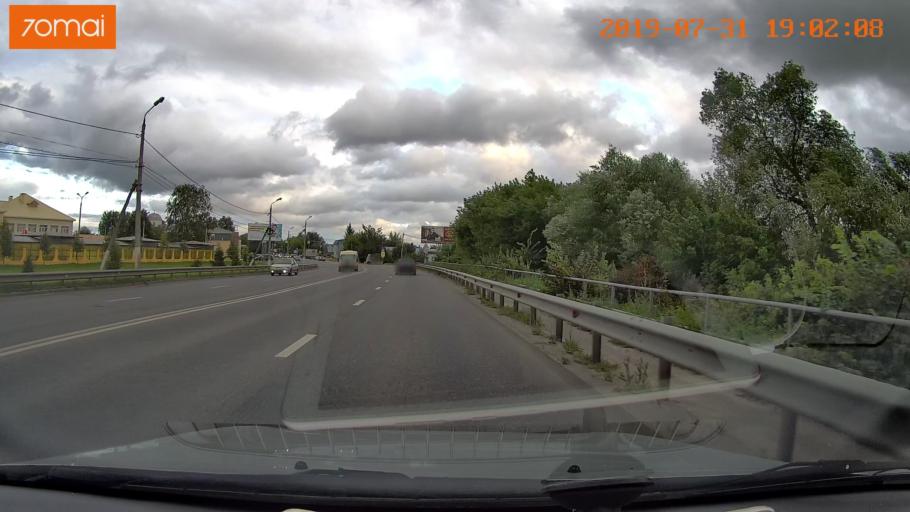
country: RU
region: Moskovskaya
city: Raduzhnyy
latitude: 55.1215
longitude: 38.7308
